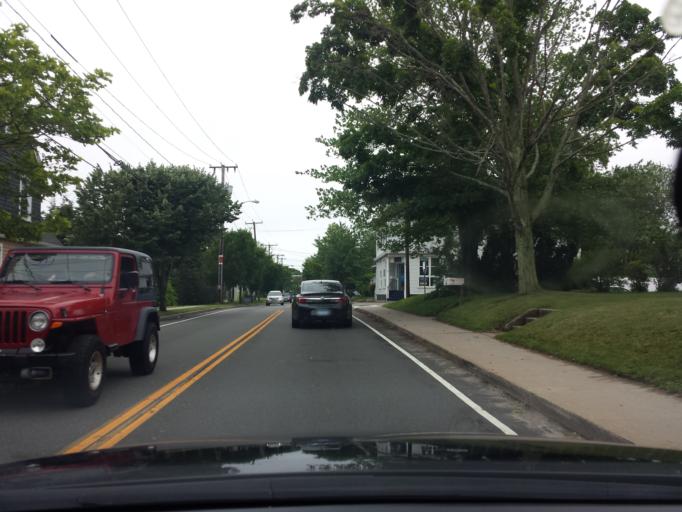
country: US
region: Connecticut
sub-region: New London County
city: Mystic
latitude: 41.3591
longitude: -71.9639
